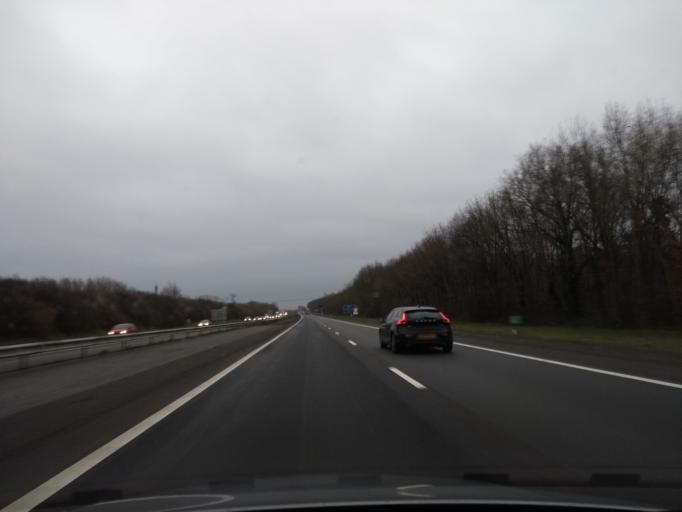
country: NL
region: Overijssel
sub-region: Gemeente Hof van Twente
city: Delden
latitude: 52.2580
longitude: 6.7521
